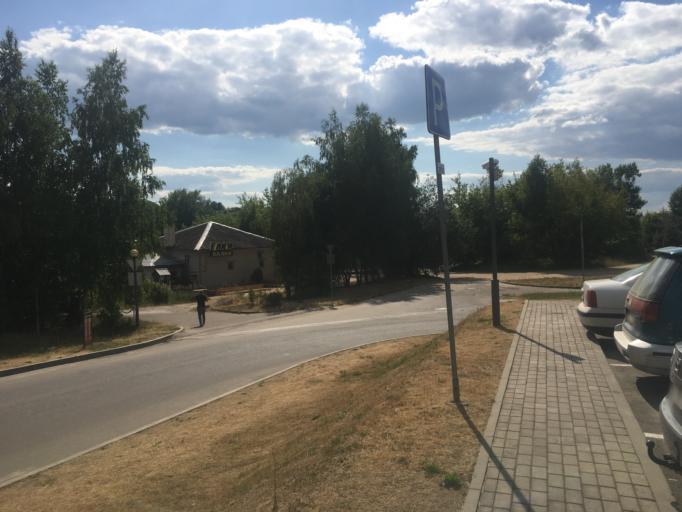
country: BY
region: Grodnenskaya
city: Hrodna
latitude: 53.6639
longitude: 23.8593
